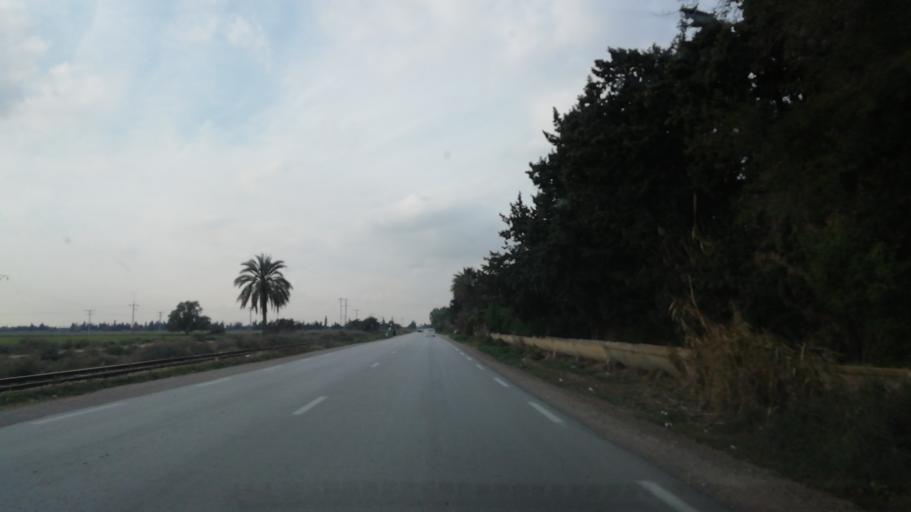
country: DZ
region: Mascara
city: Sig
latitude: 35.6603
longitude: 0.0088
